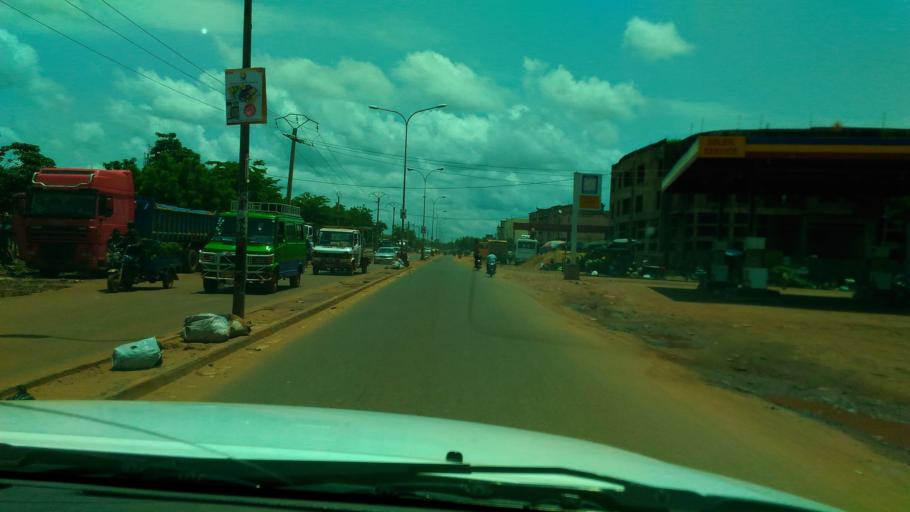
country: ML
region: Bamako
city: Bamako
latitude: 12.6680
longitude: -7.9273
